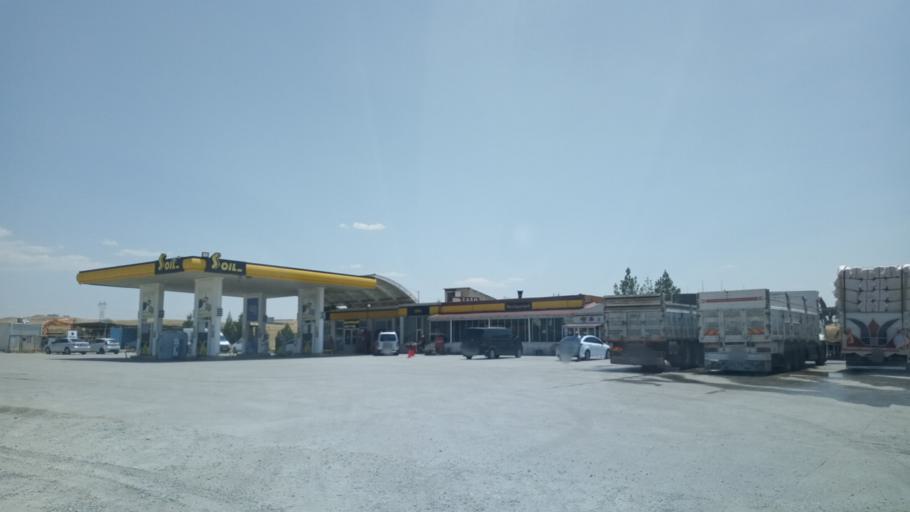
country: TR
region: Diyarbakir
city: Malabadi
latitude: 38.1341
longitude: 41.2303
